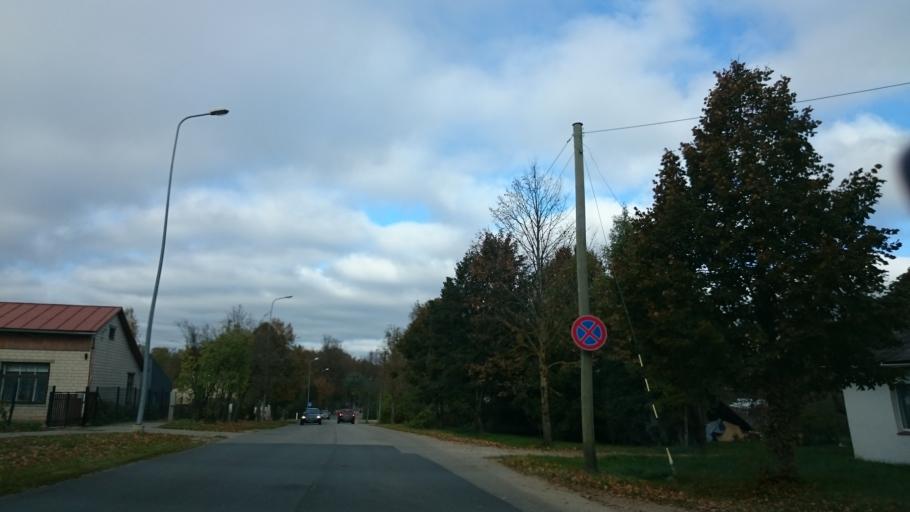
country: LV
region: Cesu Rajons
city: Cesis
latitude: 57.3029
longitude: 25.2687
